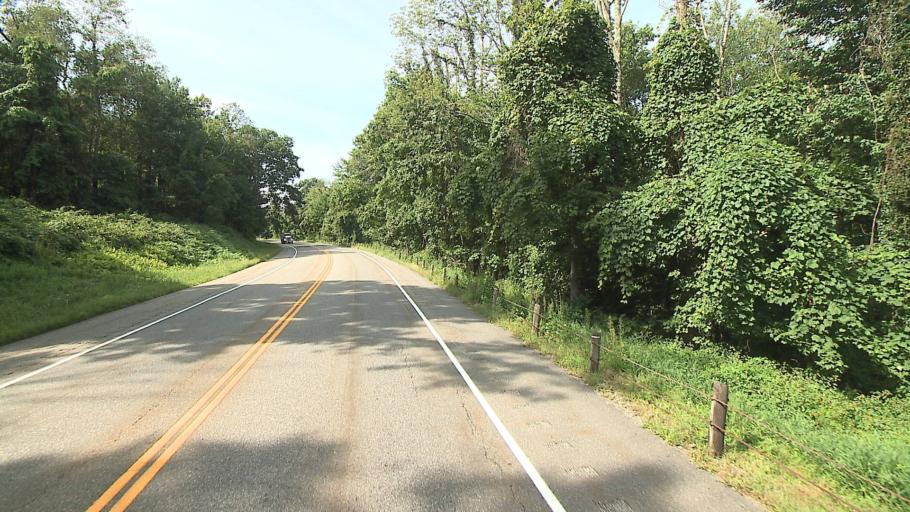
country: US
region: Connecticut
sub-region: Litchfield County
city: Litchfield
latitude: 41.7511
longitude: -73.1599
